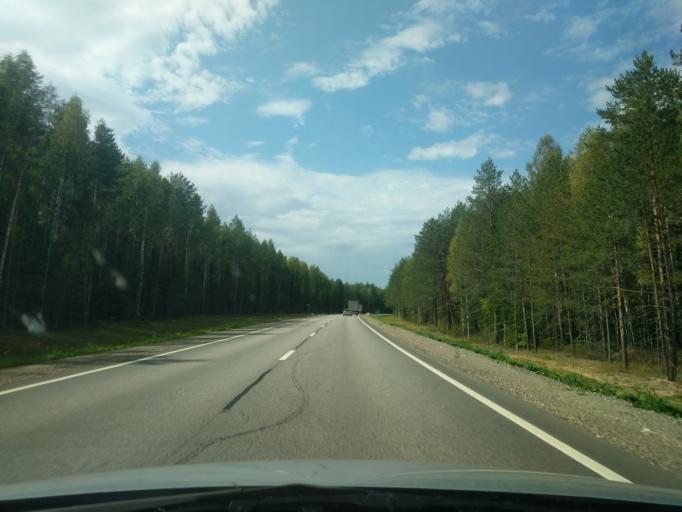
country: RU
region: Kostroma
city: Kadyy
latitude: 57.7968
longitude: 42.8506
